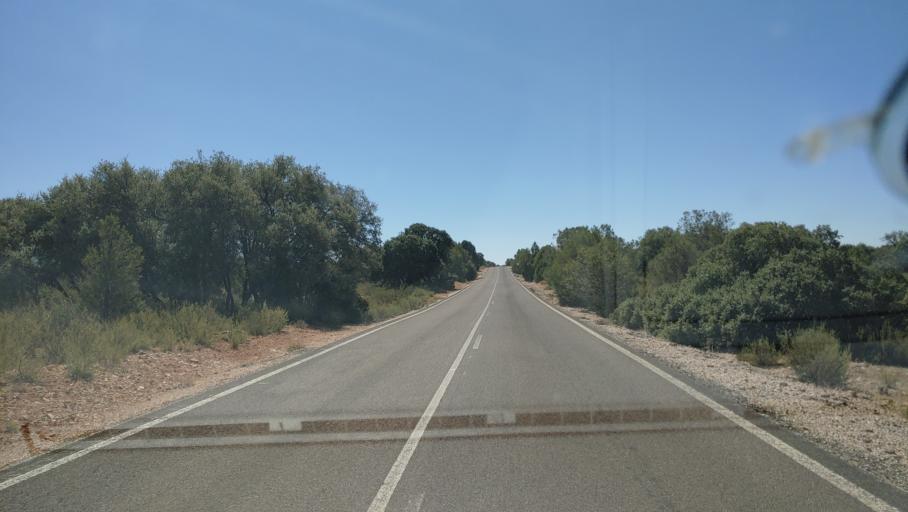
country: ES
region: Castille-La Mancha
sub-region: Provincia de Albacete
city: Ossa de Montiel
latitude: 38.8839
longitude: -2.7745
